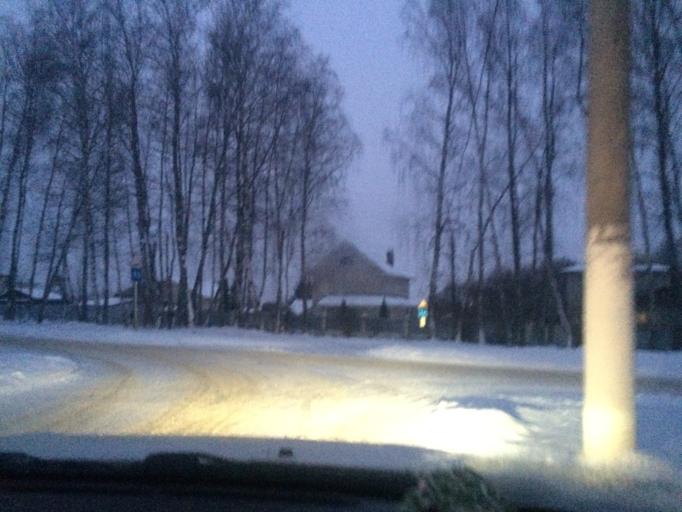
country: RU
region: Tula
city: Kosaya Gora
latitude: 54.1649
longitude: 37.4466
